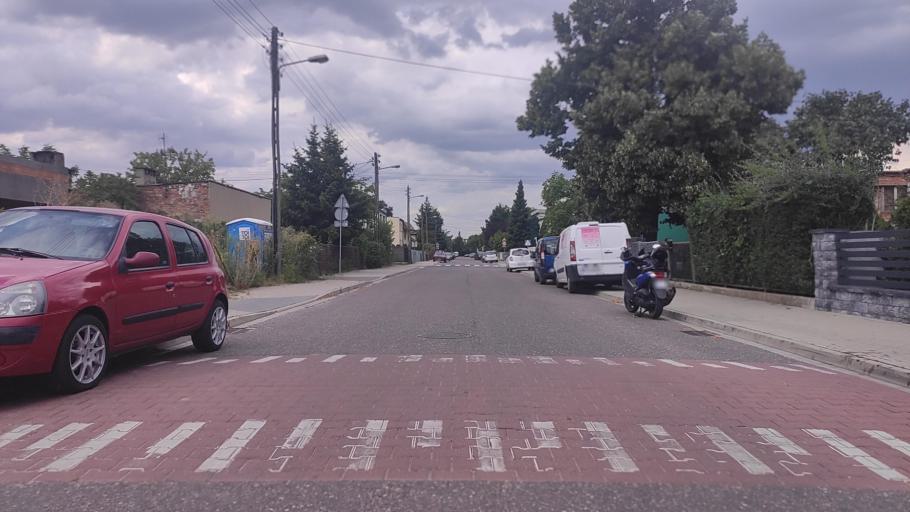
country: PL
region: Greater Poland Voivodeship
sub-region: Powiat poznanski
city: Swarzedz
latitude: 52.3986
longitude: 17.0791
